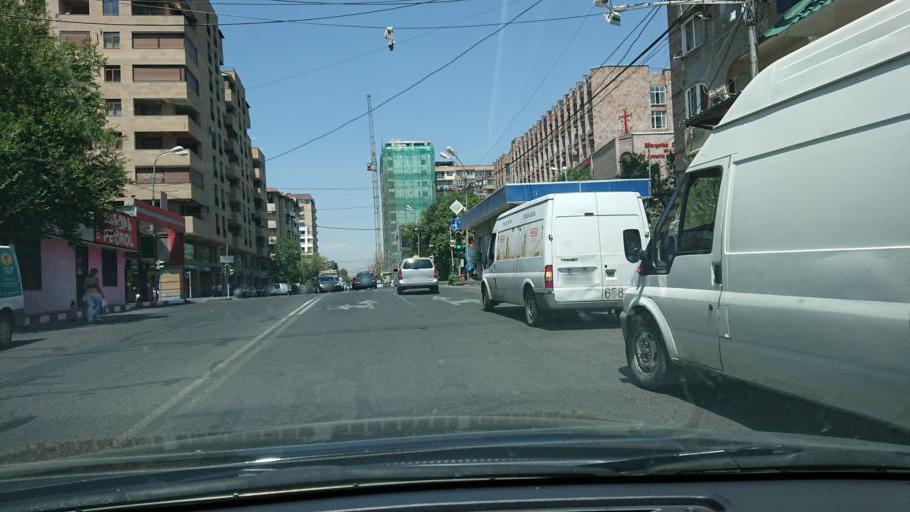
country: AM
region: Yerevan
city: Yerevan
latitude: 40.1983
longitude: 44.5019
